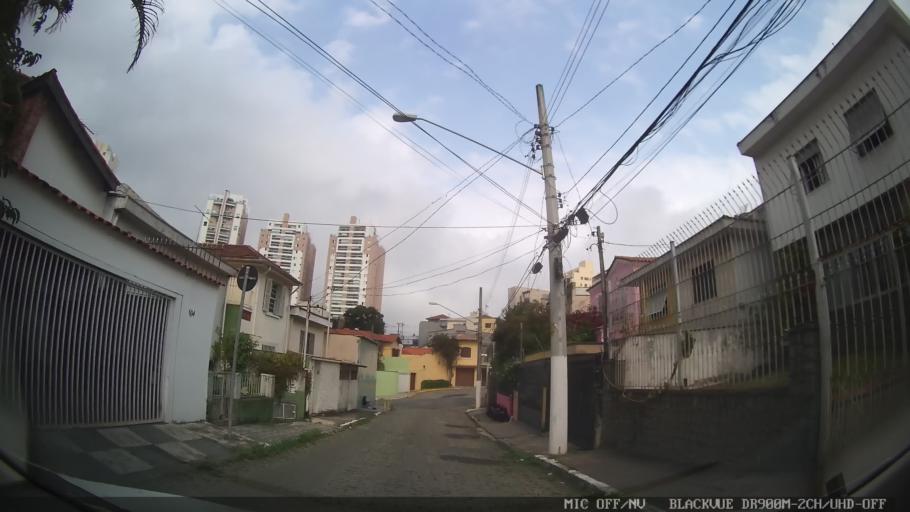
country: BR
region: Sao Paulo
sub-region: Sao Paulo
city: Sao Paulo
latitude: -23.5869
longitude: -46.6306
